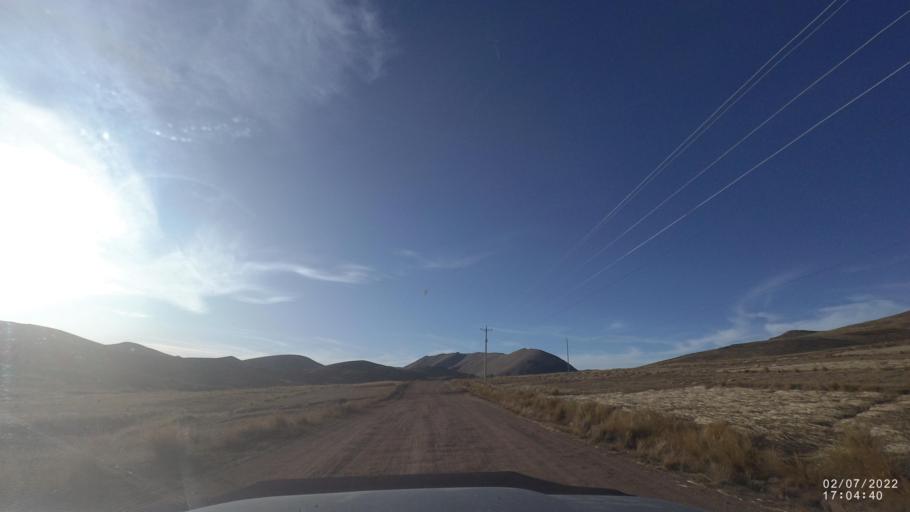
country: BO
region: Cochabamba
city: Irpa Irpa
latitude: -17.9134
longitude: -66.5595
